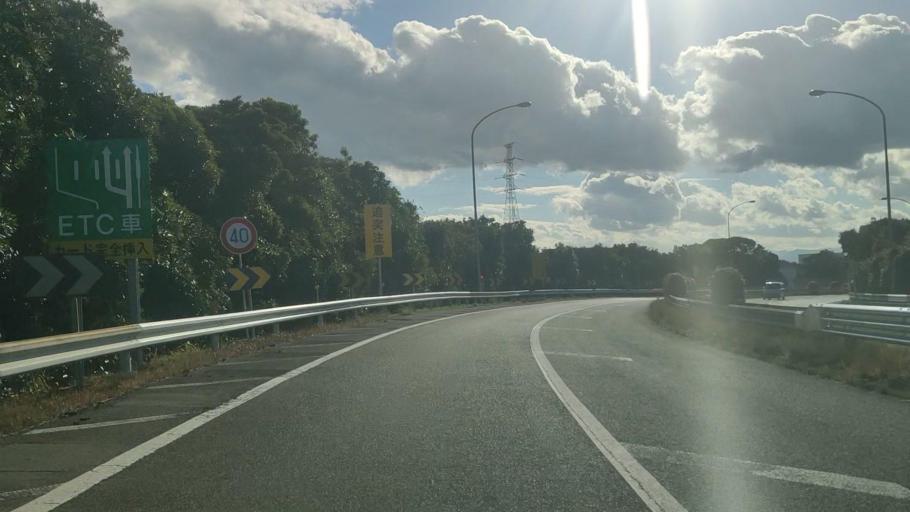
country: JP
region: Fukuoka
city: Nogata
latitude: 33.7836
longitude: 130.7462
